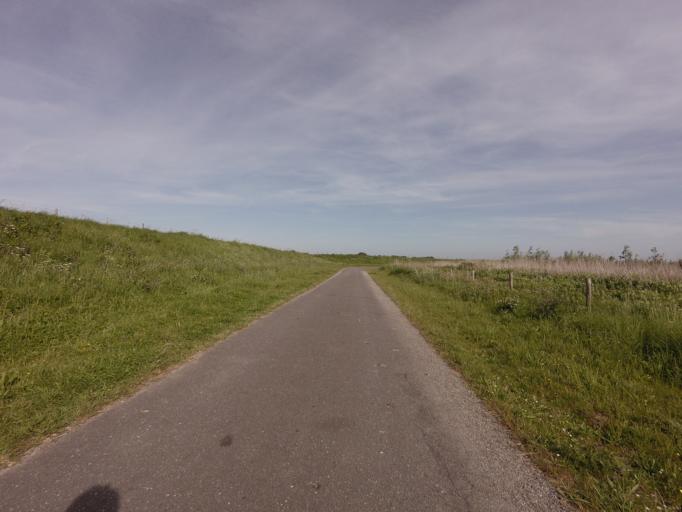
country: NL
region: North Brabant
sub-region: Gemeente Steenbergen
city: Dinteloord
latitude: 51.7383
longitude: 4.3414
